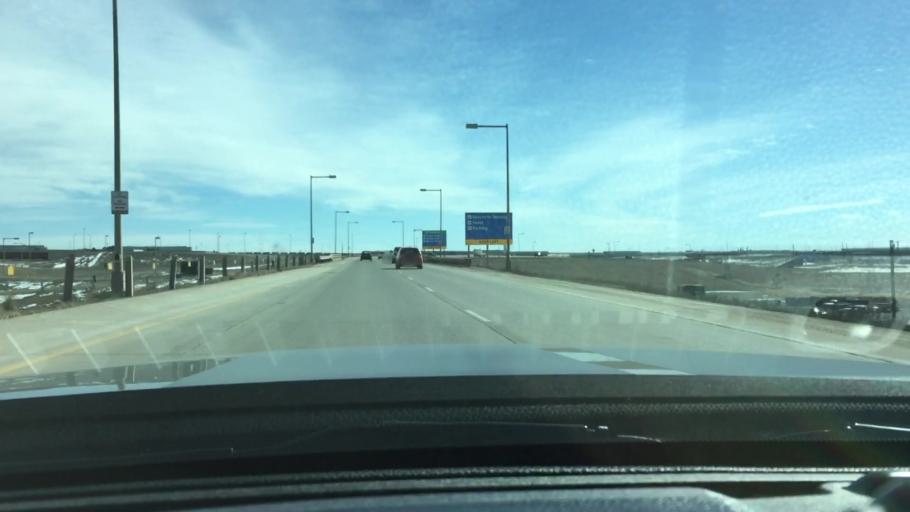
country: US
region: Colorado
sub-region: Weld County
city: Lochbuie
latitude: 39.8439
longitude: -104.6786
